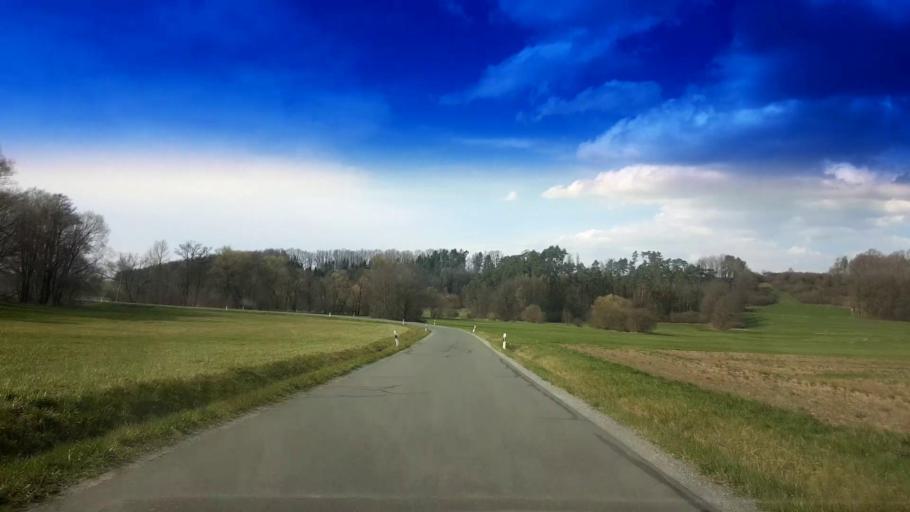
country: DE
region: Bavaria
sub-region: Upper Franconia
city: Gesees
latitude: 50.0300
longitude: 11.6392
